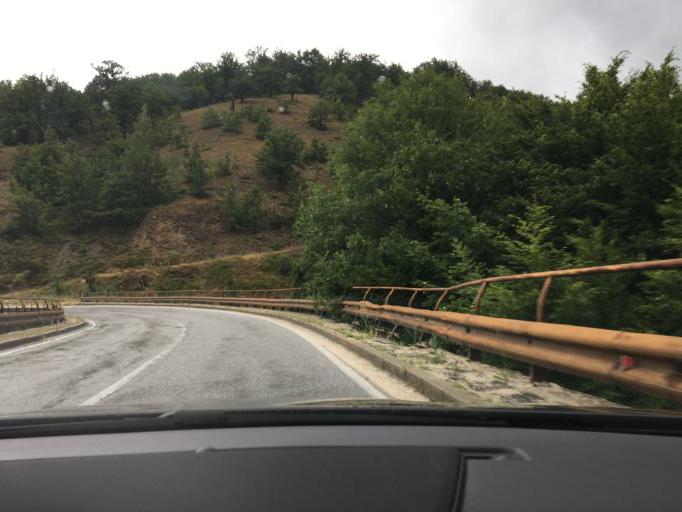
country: MK
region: Kriva Palanka
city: Kriva Palanka
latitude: 42.2204
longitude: 22.4334
